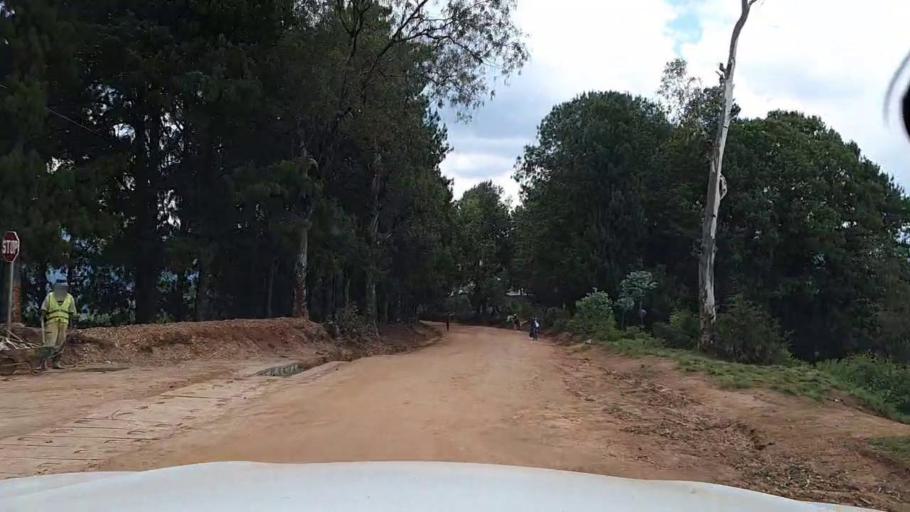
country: RW
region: Southern Province
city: Nzega
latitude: -2.7083
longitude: 29.5190
